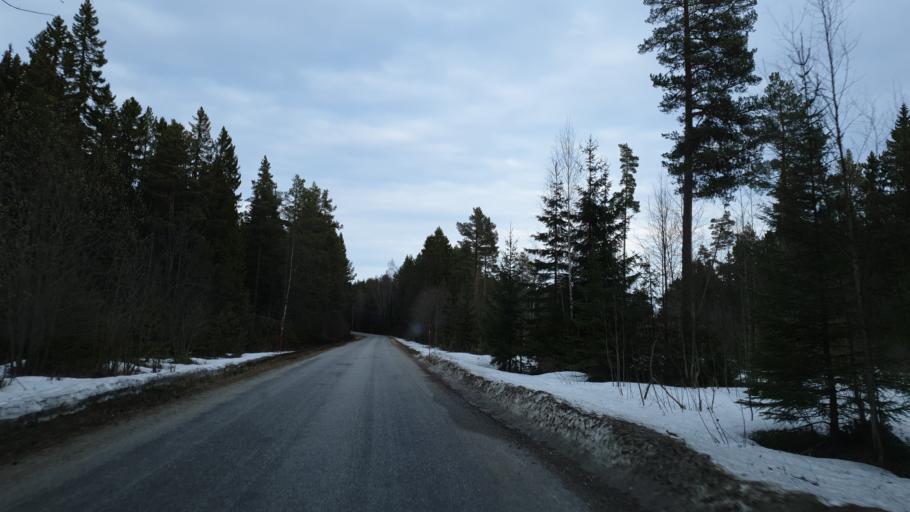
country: SE
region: Vaesternorrland
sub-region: Sundsvalls Kommun
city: Njurundabommen
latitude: 61.9624
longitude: 17.3658
